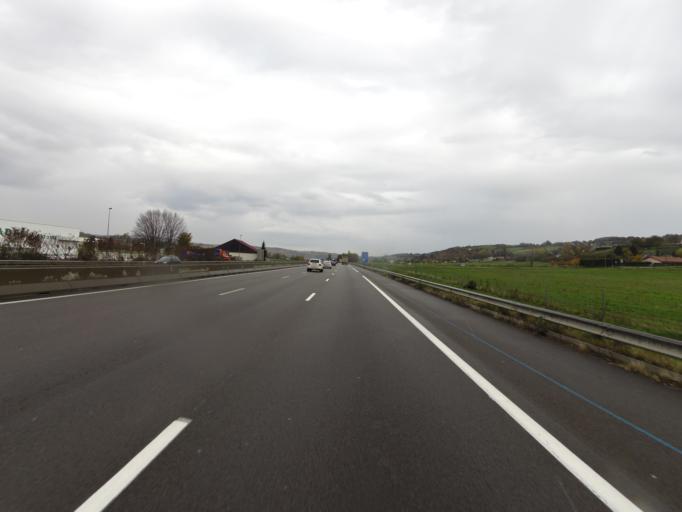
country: FR
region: Rhone-Alpes
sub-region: Departement de l'Isere
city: Reventin-Vaugris
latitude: 45.4644
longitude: 4.8331
